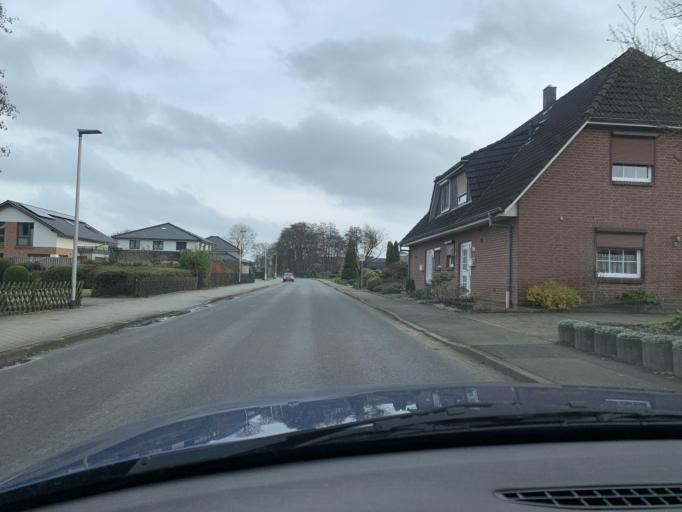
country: DE
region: Schleswig-Holstein
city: Wesseln
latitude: 54.2052
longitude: 9.0818
